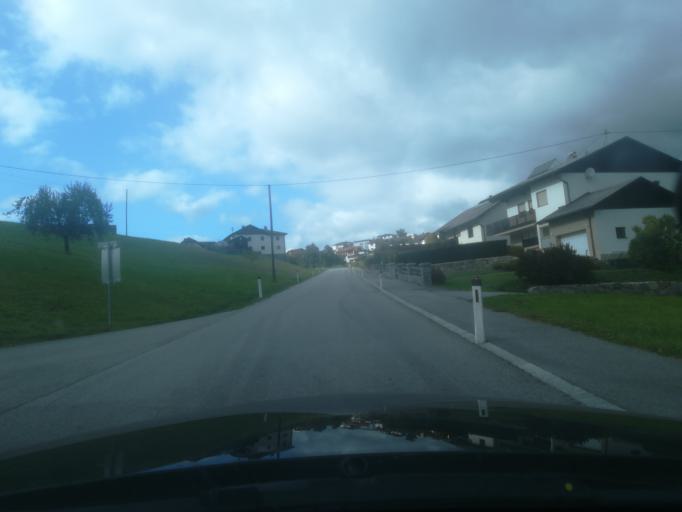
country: AT
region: Upper Austria
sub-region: Politischer Bezirk Urfahr-Umgebung
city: Herzogsdorf
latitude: 48.4266
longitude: 14.1367
